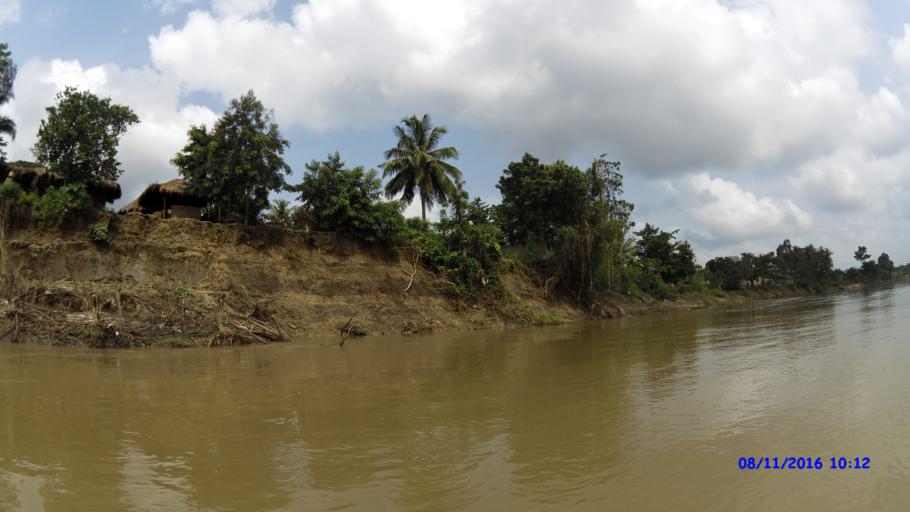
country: BJ
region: Mono
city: Come
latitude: 6.4544
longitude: 1.7528
